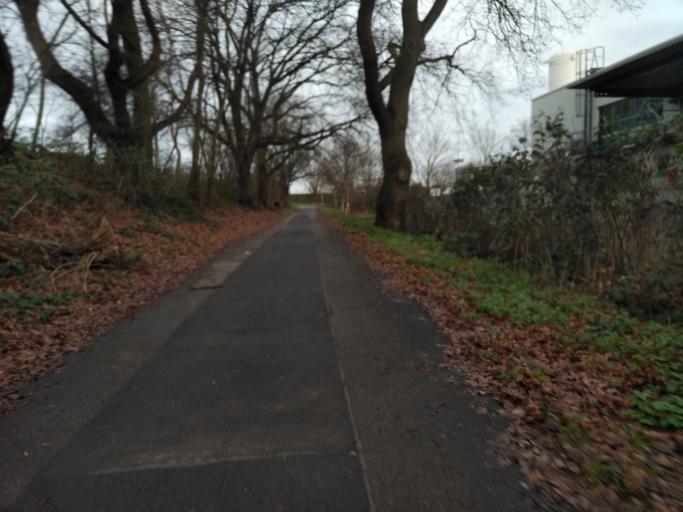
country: DE
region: North Rhine-Westphalia
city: Opladen
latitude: 51.0558
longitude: 7.0113
